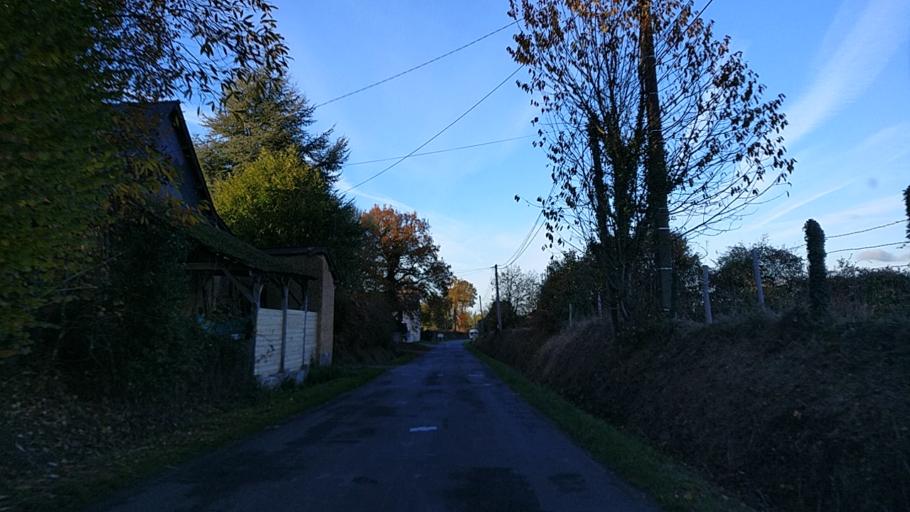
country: FR
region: Brittany
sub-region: Departement d'Ille-et-Vilaine
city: Saint-Sulpice-la-Foret
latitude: 48.2100
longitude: -1.5796
